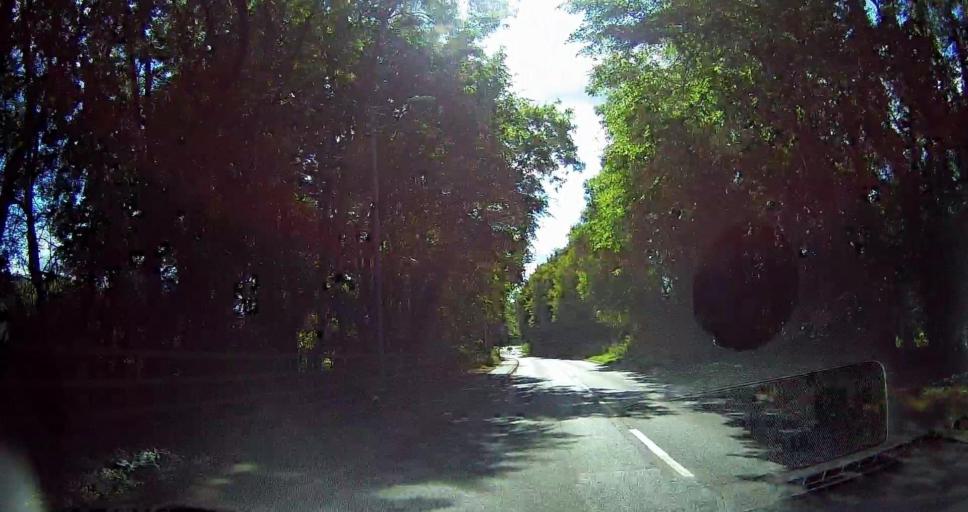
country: GB
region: England
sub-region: Staffordshire
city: Stone
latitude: 52.9168
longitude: -2.1655
